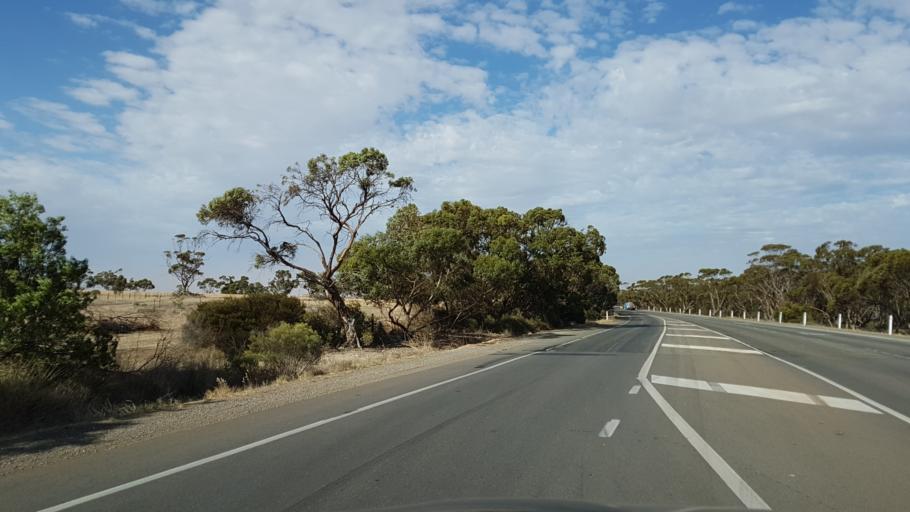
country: AU
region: South Australia
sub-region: Wakefield
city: Balaklava
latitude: -34.0939
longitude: 138.4992
